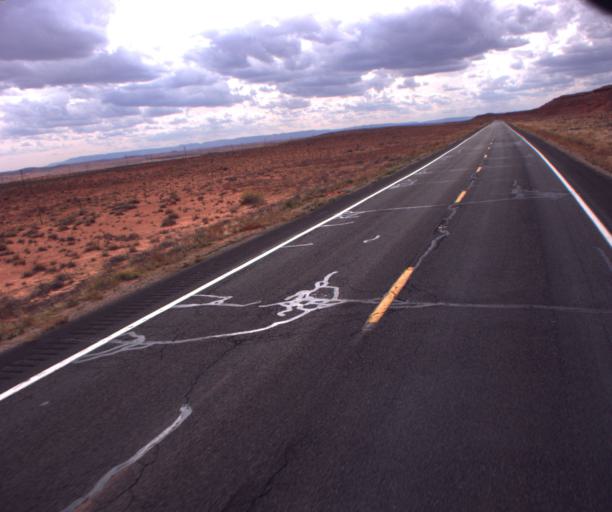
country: US
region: Arizona
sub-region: Navajo County
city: Kayenta
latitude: 36.9109
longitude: -109.7814
